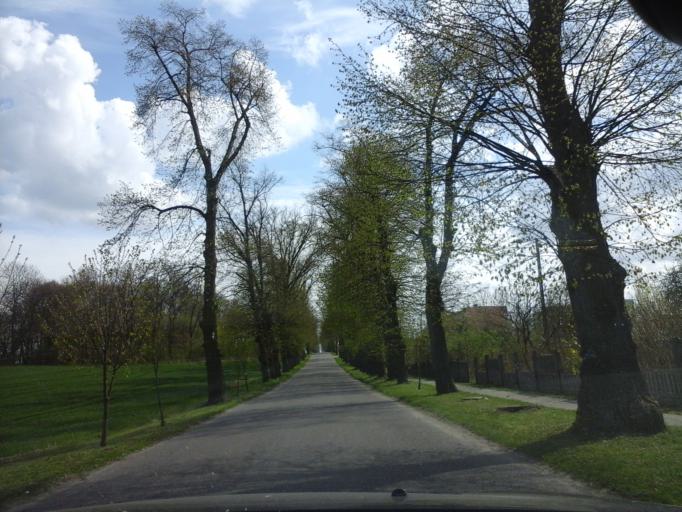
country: PL
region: West Pomeranian Voivodeship
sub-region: Powiat choszczenski
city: Pelczyce
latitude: 53.0986
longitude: 15.3472
